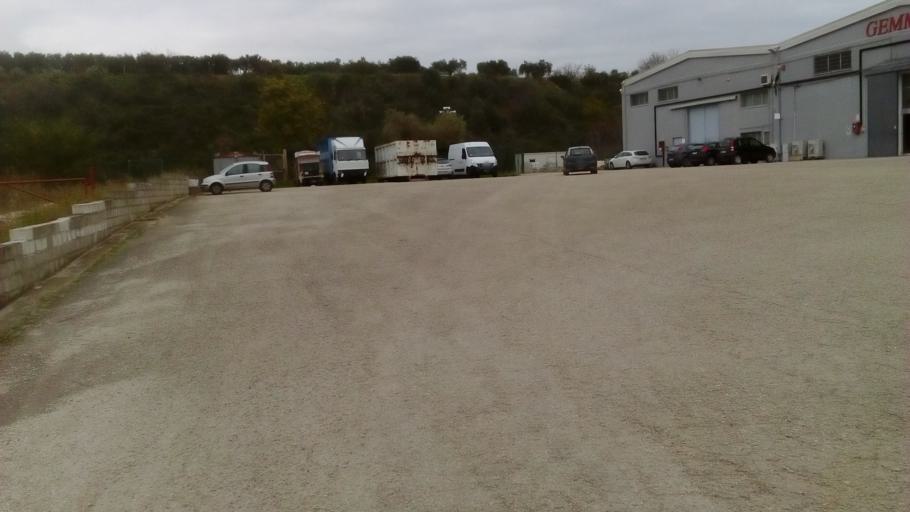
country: IT
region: Abruzzo
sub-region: Provincia di Chieti
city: San Salvo
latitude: 42.0275
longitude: 14.7373
